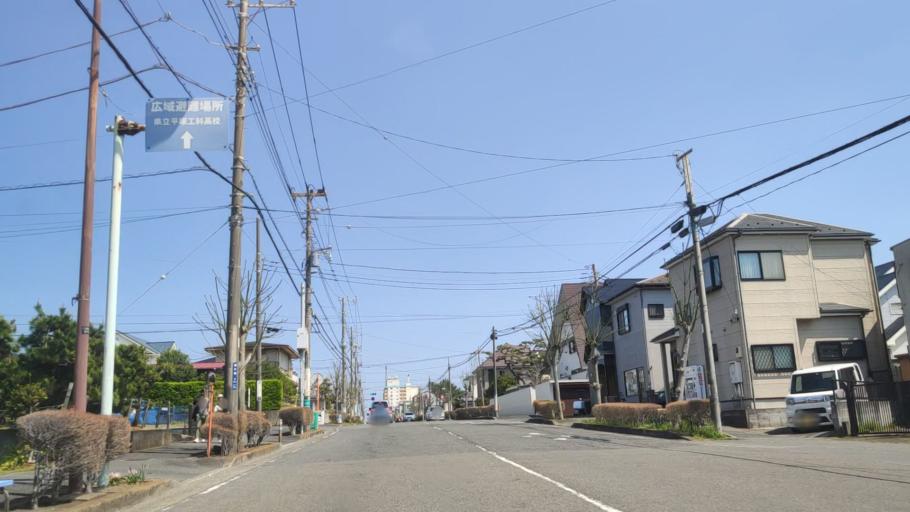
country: JP
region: Kanagawa
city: Hiratsuka
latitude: 35.3173
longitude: 139.3325
